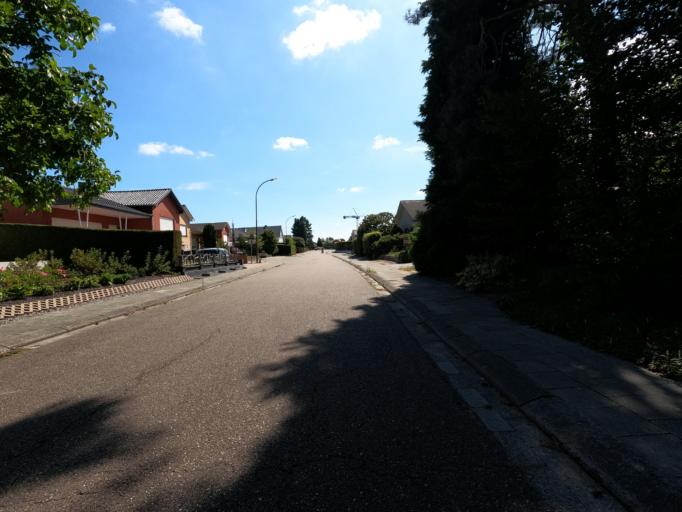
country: BE
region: Flanders
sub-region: Provincie Vlaams-Brabant
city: Scherpenheuvel-Zichem
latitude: 51.0232
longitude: 4.9919
